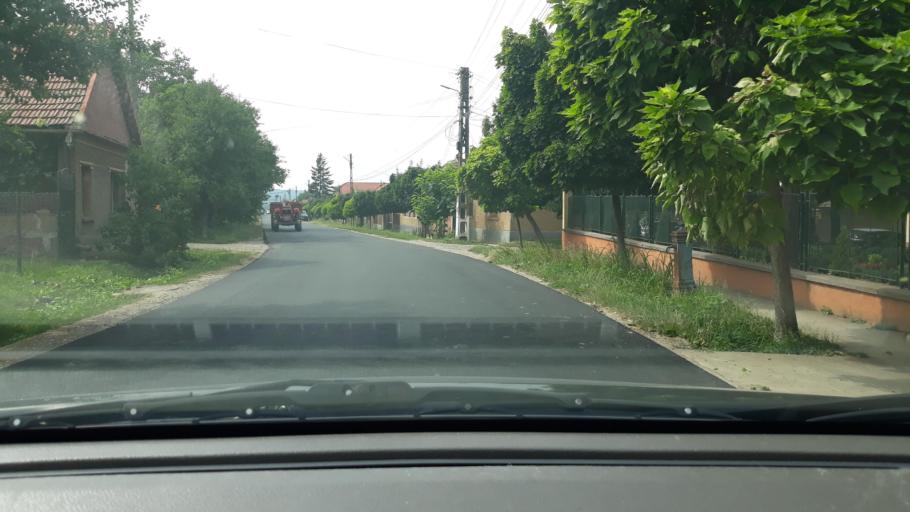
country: RO
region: Bihor
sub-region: Comuna Chislaz
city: Misca
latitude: 47.2657
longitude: 22.2539
